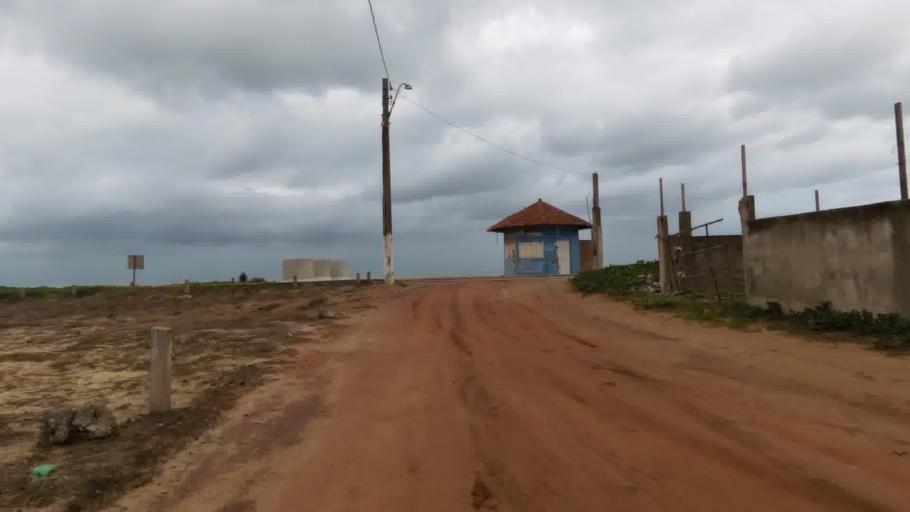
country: BR
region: Espirito Santo
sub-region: Marataizes
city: Marataizes
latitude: -21.0710
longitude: -40.8374
